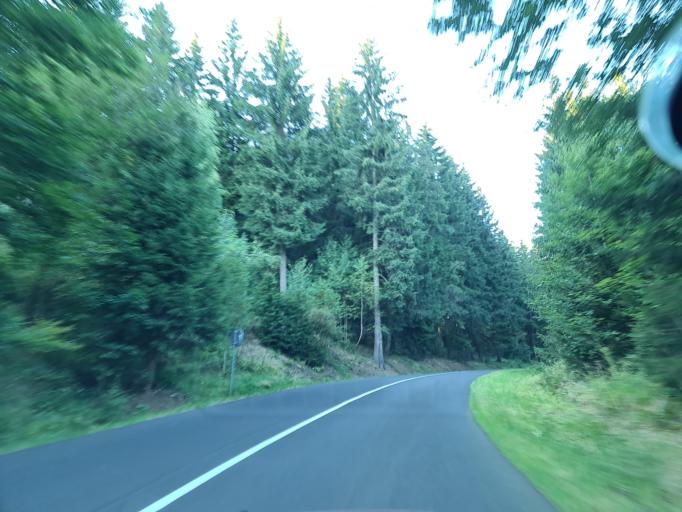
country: DE
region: Saxony
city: Seiffen
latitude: 50.6188
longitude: 13.4097
